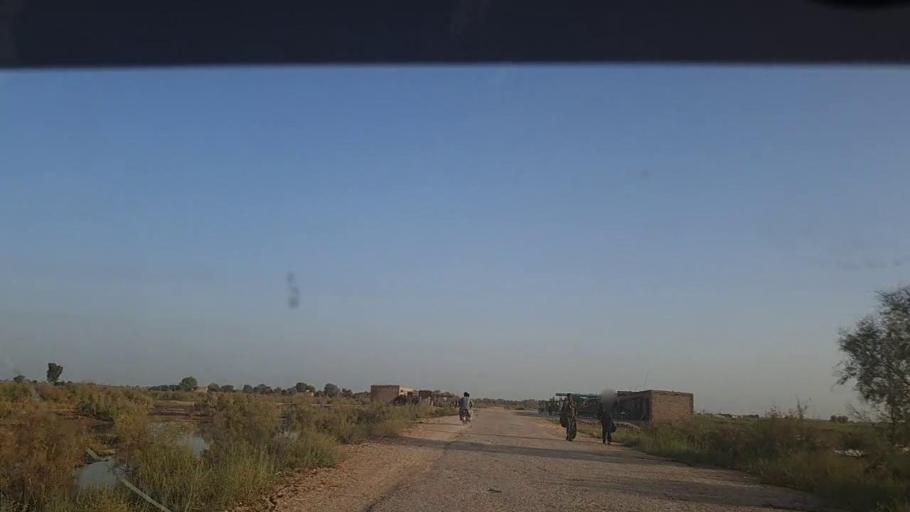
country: PK
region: Sindh
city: Thul
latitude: 28.1503
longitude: 68.8866
